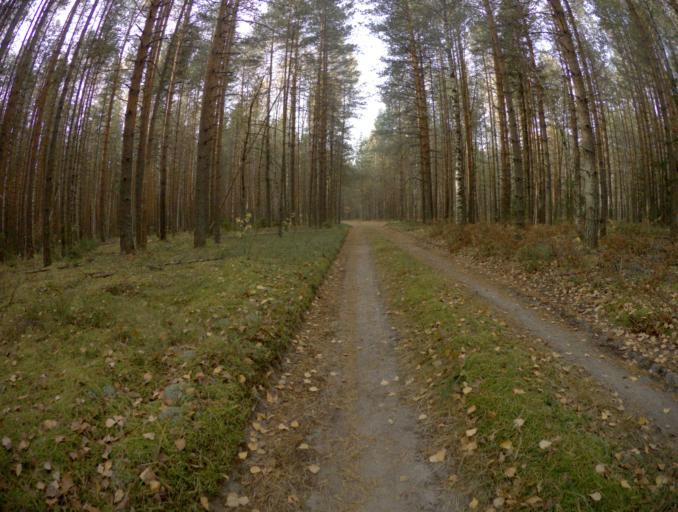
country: RU
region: Vladimir
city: Vorsha
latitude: 55.9549
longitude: 40.1402
